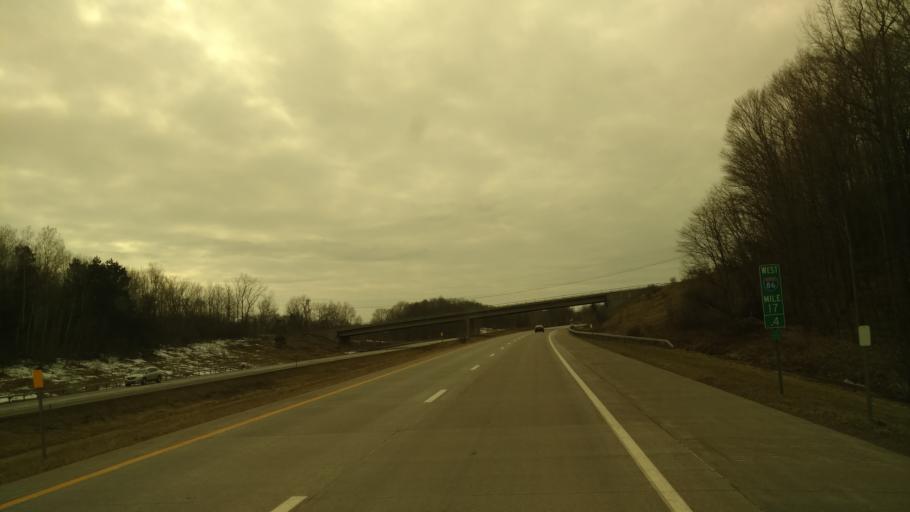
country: US
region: New York
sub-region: Chautauqua County
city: Lakewood
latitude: 42.1533
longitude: -79.4350
